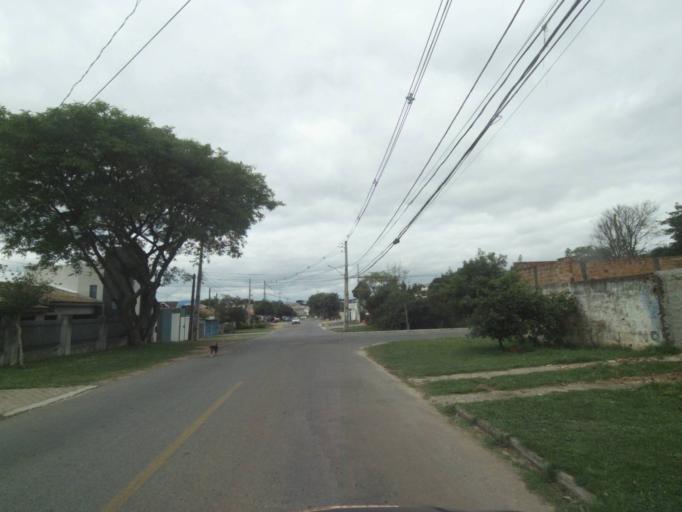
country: BR
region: Parana
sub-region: Sao Jose Dos Pinhais
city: Sao Jose dos Pinhais
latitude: -25.5527
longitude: -49.2564
